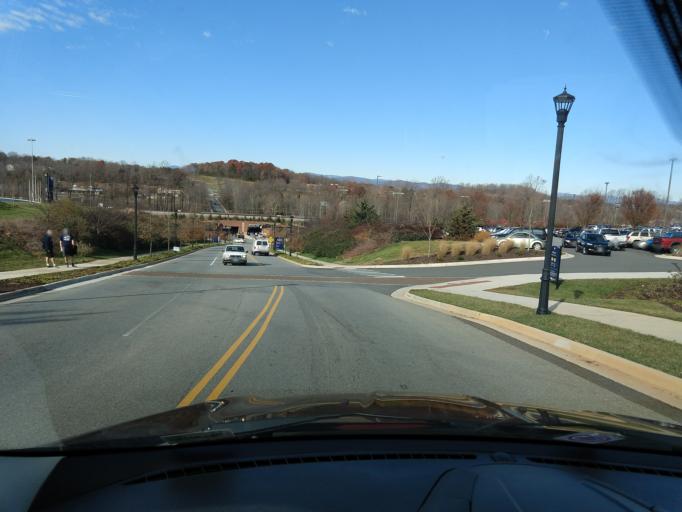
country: US
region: Virginia
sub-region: City of Lynchburg
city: West Lynchburg
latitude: 37.3545
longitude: -79.1780
